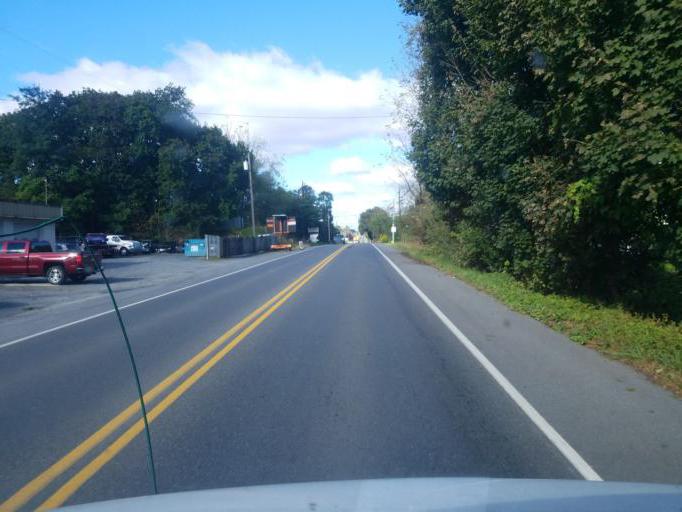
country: US
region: Pennsylvania
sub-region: Franklin County
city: Waynesboro
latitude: 39.7653
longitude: -77.6111
